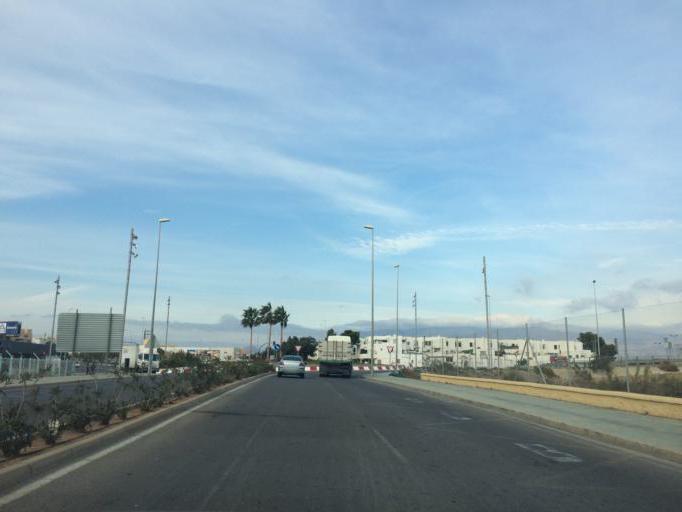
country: ES
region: Andalusia
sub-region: Provincia de Almeria
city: Almeria
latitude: 36.8424
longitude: -2.4322
